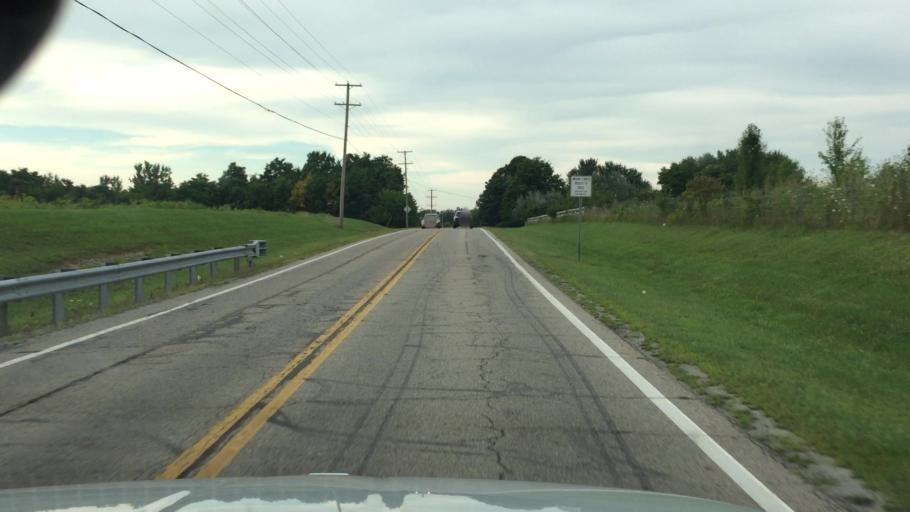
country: US
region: Ohio
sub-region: Franklin County
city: Lake Darby
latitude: 40.0256
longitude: -83.2619
